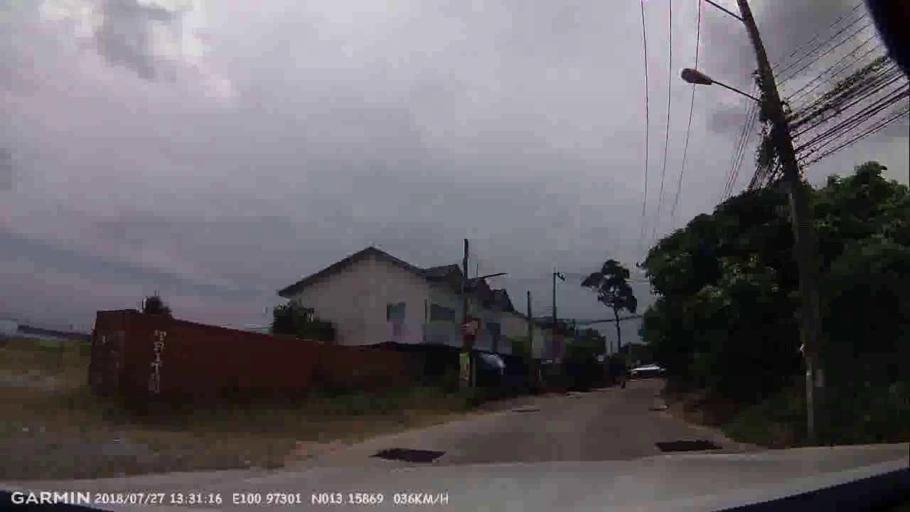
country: TH
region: Chon Buri
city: Si Racha
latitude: 13.1588
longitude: 100.9730
